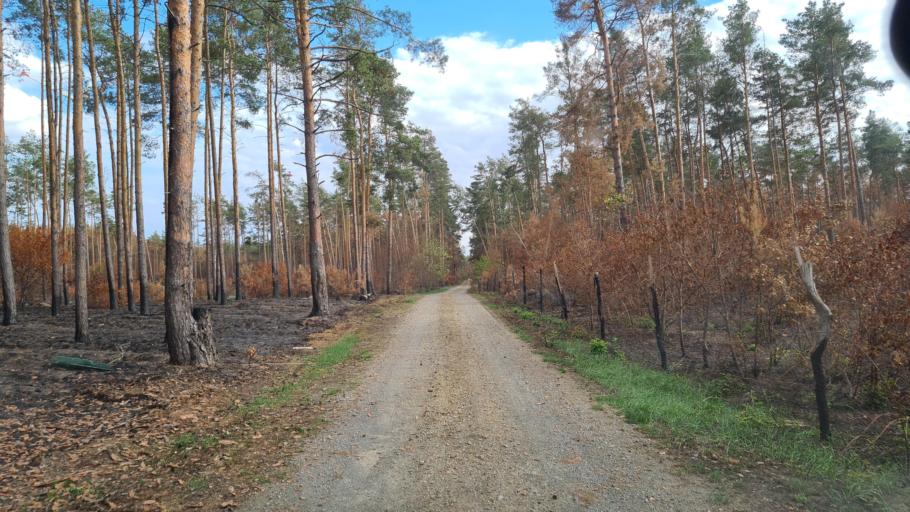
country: DE
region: Saxony
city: Arzberg
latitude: 51.5627
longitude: 13.1831
